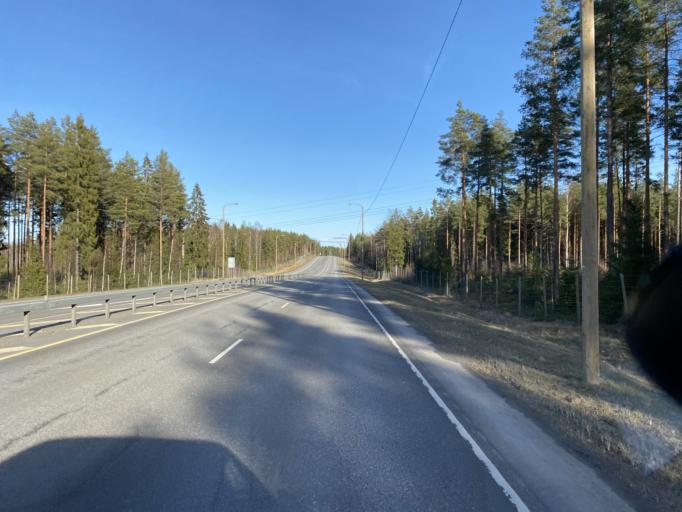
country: FI
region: Satakunta
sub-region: Pori
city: Huittinen
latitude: 61.1757
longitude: 22.6249
